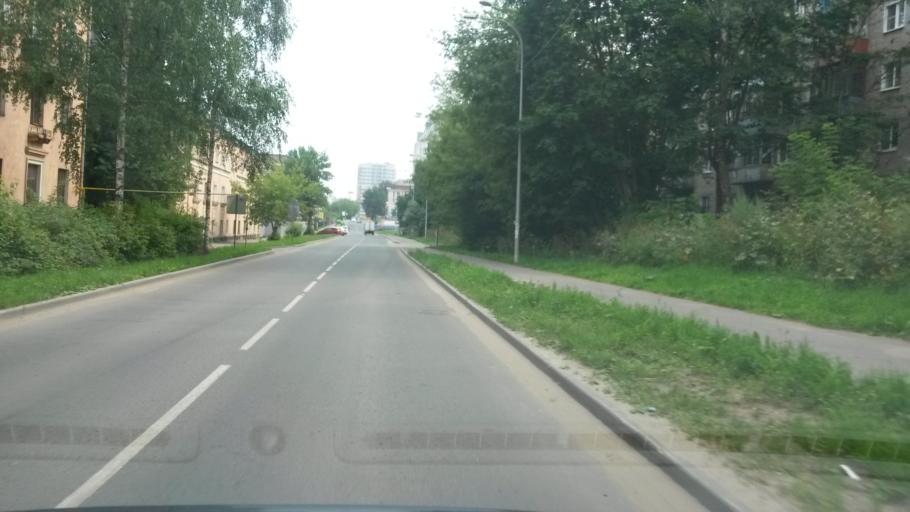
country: RU
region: Ivanovo
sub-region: Gorod Ivanovo
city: Ivanovo
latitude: 57.0041
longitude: 40.9640
